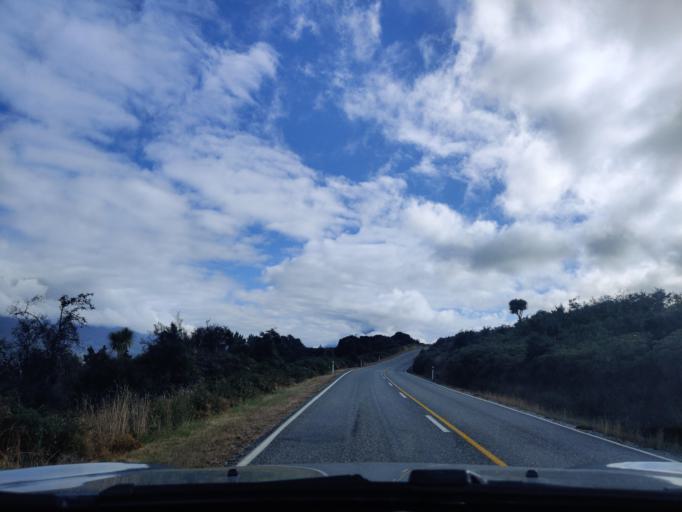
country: NZ
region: Otago
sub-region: Queenstown-Lakes District
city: Queenstown
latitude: -44.8795
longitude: 168.3999
